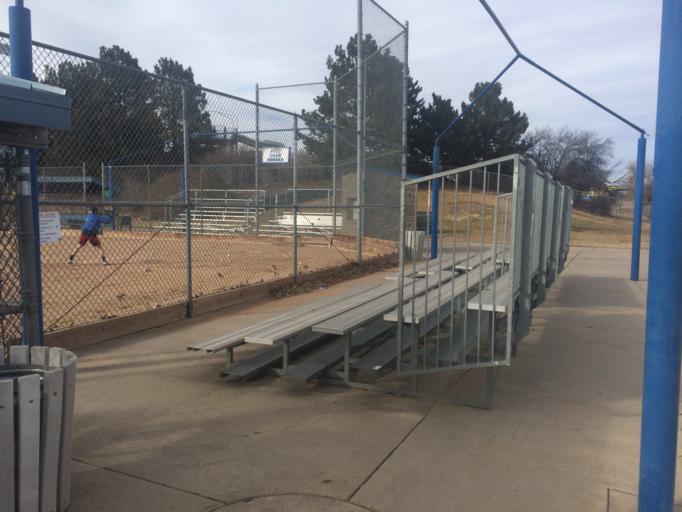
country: US
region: Colorado
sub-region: Broomfield County
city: Broomfield
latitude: 39.9185
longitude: -105.0649
